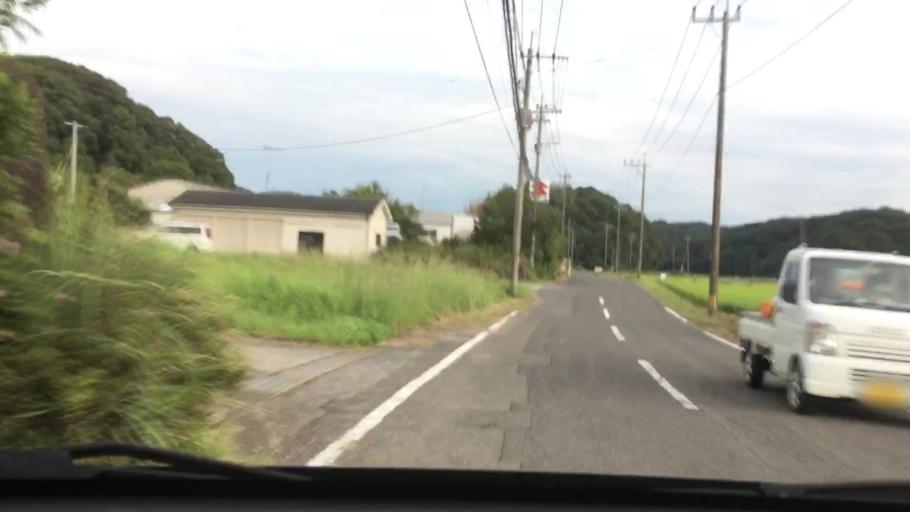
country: JP
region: Nagasaki
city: Sasebo
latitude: 32.9948
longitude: 129.7702
